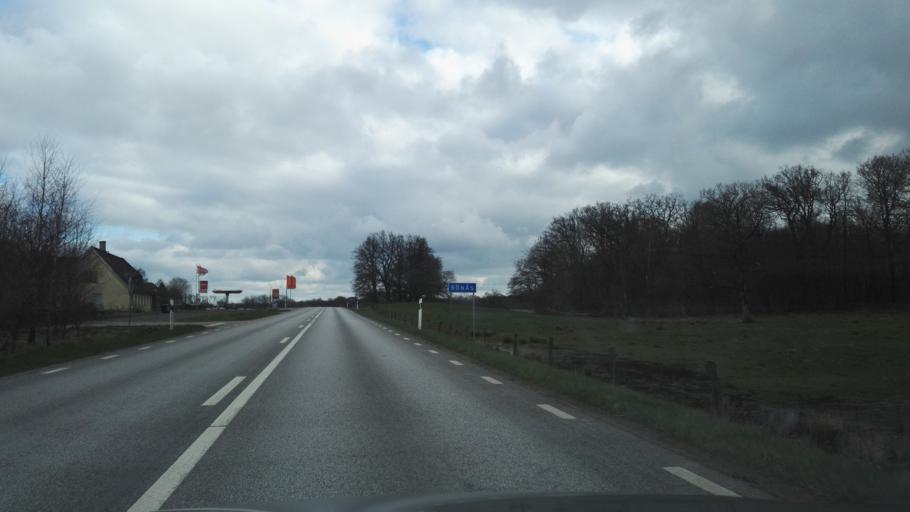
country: SE
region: Skane
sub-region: Sjobo Kommun
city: Sjoebo
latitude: 55.7384
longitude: 13.7027
